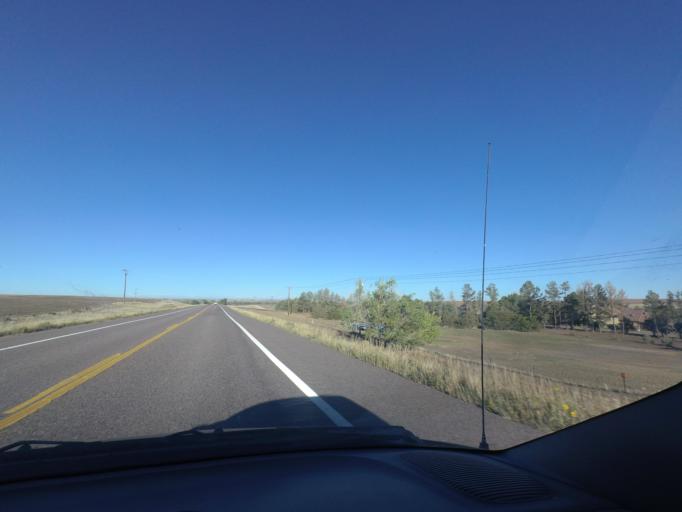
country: US
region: Colorado
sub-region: Arapahoe County
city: Byers
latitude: 39.7399
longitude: -104.0848
